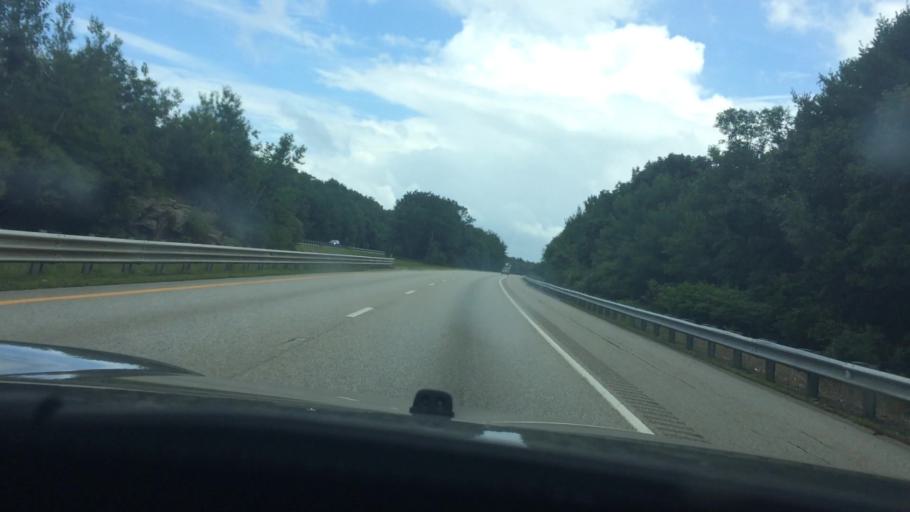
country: US
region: Massachusetts
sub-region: Worcester County
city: Westminster
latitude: 42.5573
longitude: -71.9263
